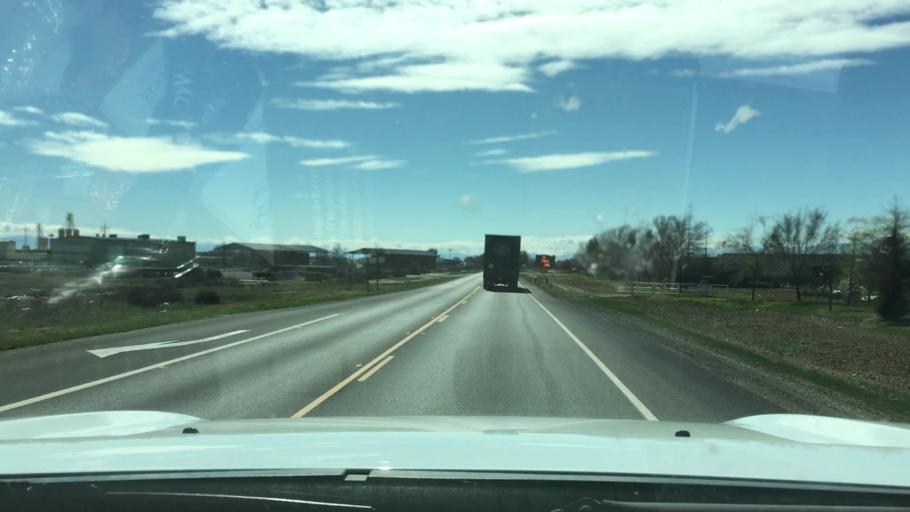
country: US
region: California
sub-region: Kern County
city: Shafter
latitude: 35.4556
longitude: -119.2597
